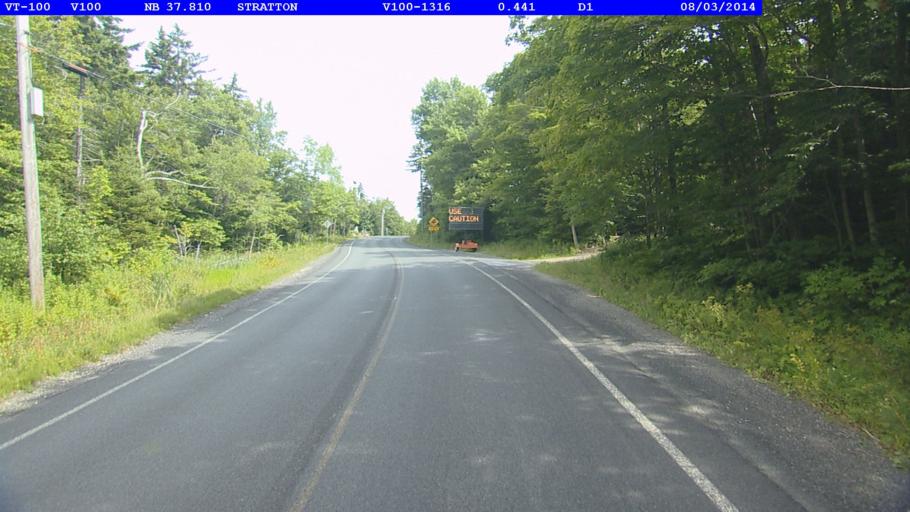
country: US
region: Vermont
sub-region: Windham County
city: Dover
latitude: 42.9976
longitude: -72.8871
